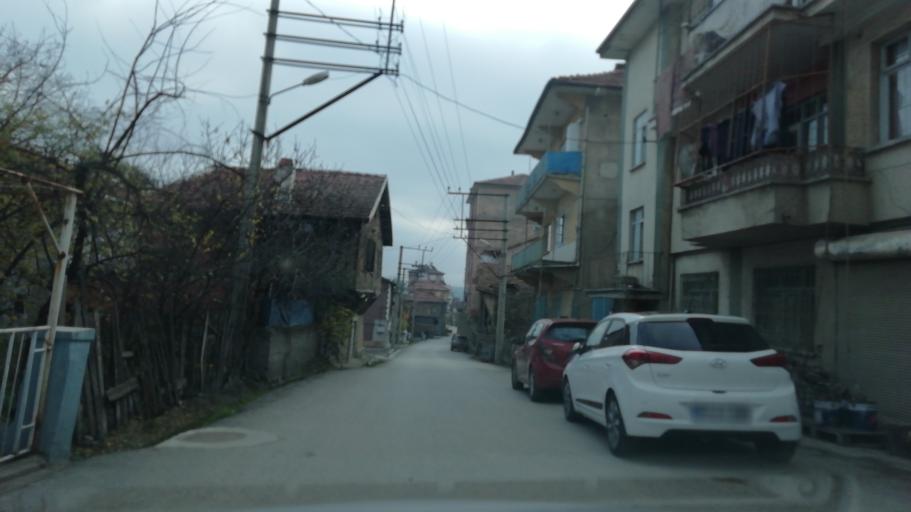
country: TR
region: Karabuk
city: Karabuk
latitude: 41.2216
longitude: 32.6270
